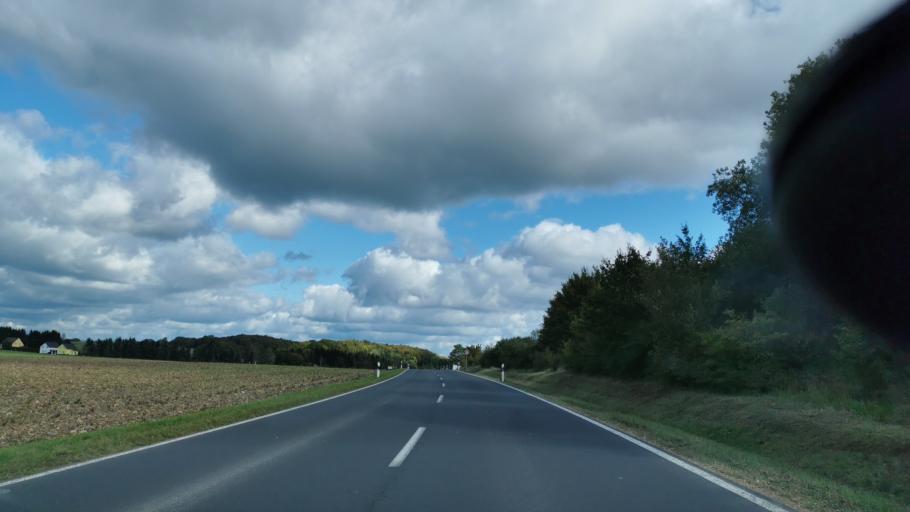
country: DE
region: Rheinland-Pfalz
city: Uxheim
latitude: 50.3205
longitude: 6.7310
